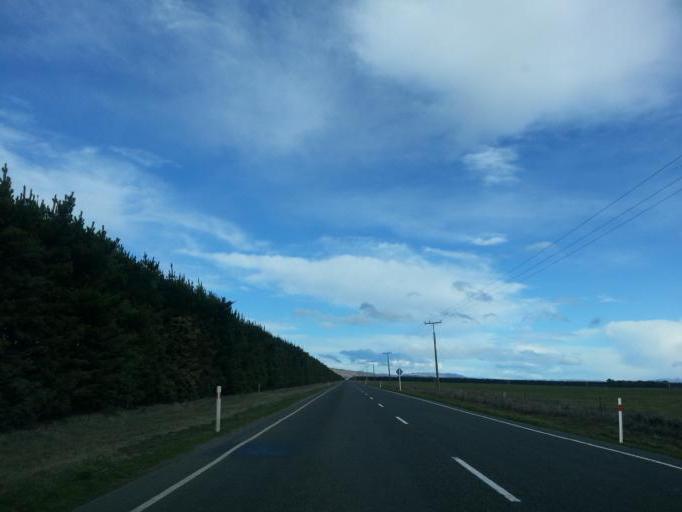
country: NZ
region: Canterbury
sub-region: Hurunui District
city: Amberley
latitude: -42.8023
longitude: 172.8257
